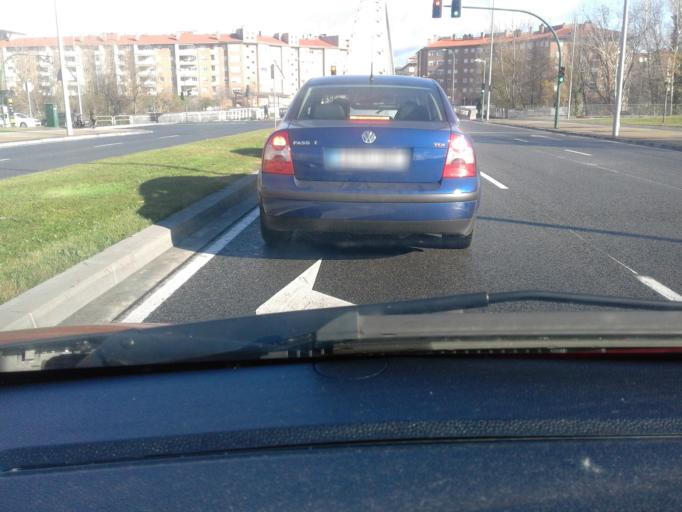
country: ES
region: Navarre
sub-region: Provincia de Navarra
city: Primer Ensanche
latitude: 42.8219
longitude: -1.6556
